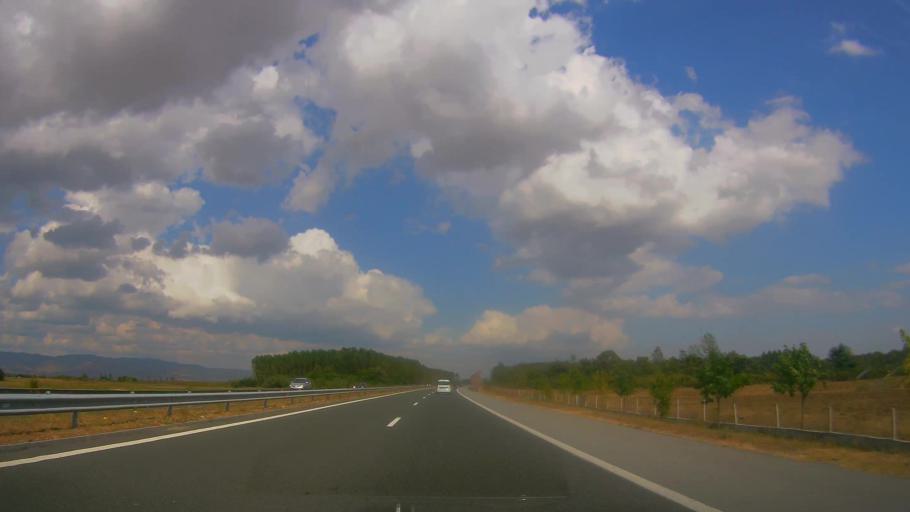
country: BG
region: Yambol
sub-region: Obshtina Yambol
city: Yambol
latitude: 42.5474
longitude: 26.4954
